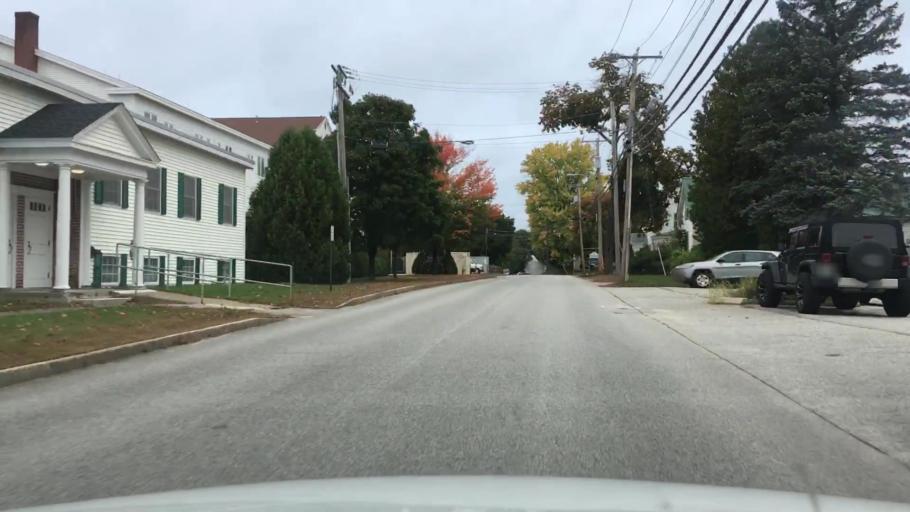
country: US
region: Maine
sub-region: Oxford County
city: Norway
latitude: 44.2106
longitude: -70.5318
